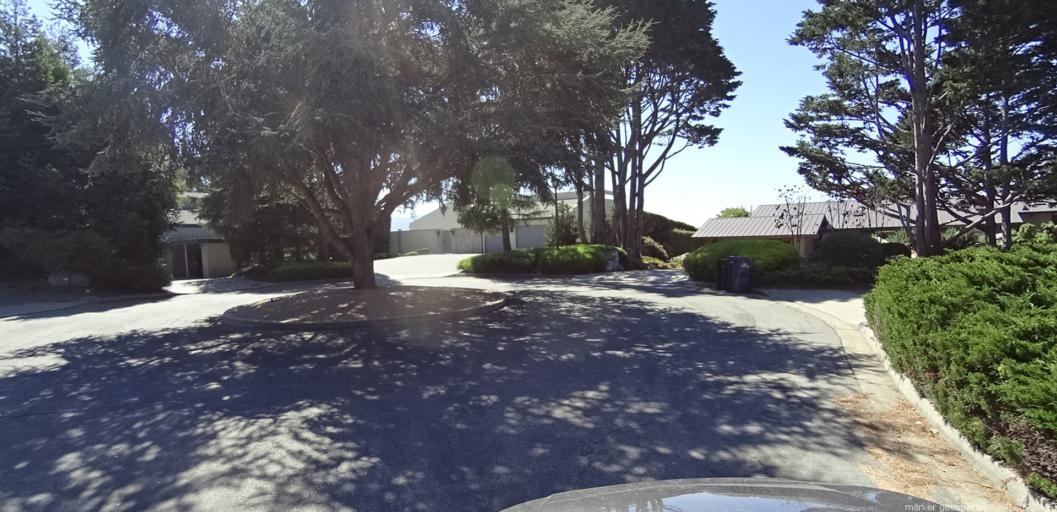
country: US
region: California
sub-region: Monterey County
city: Carmel-by-the-Sea
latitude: 36.5640
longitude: -121.9080
